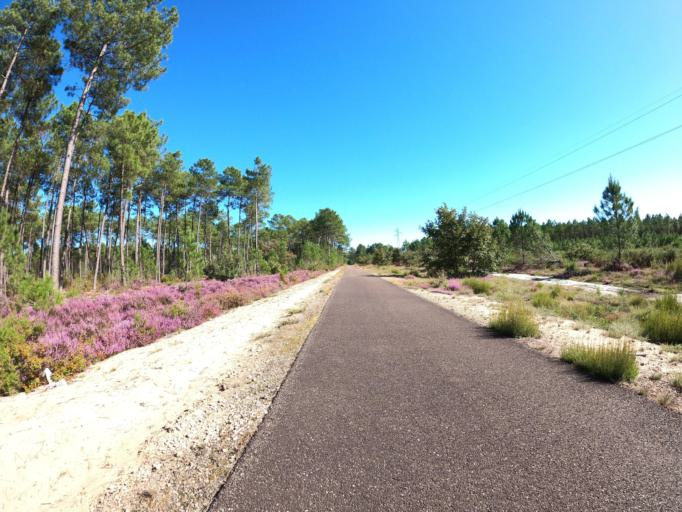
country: FR
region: Aquitaine
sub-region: Departement des Landes
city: Ychoux
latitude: 44.3371
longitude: -0.9530
